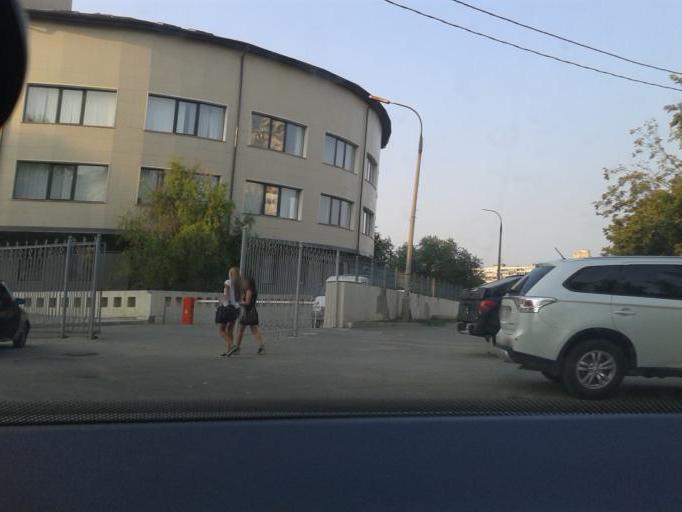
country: RU
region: Volgograd
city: Volgograd
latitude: 48.6990
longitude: 44.5078
